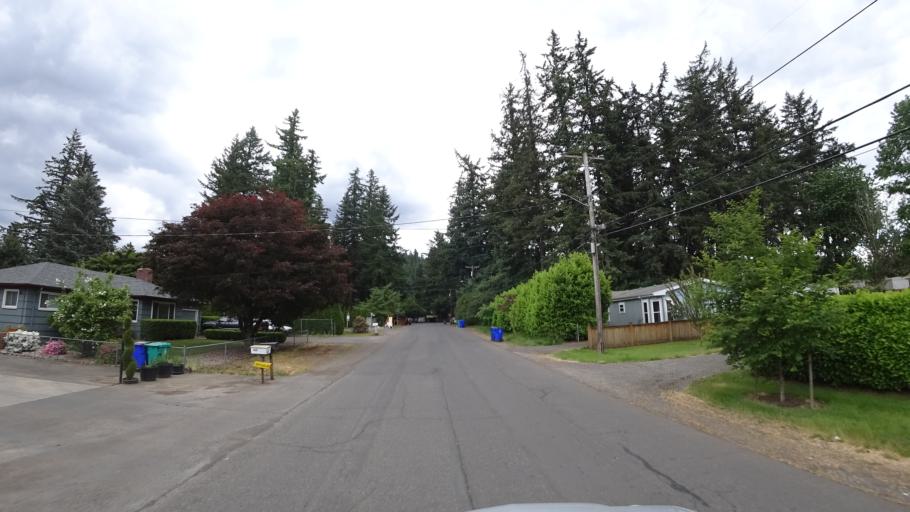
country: US
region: Oregon
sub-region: Clackamas County
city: Happy Valley
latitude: 45.4971
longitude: -122.5023
